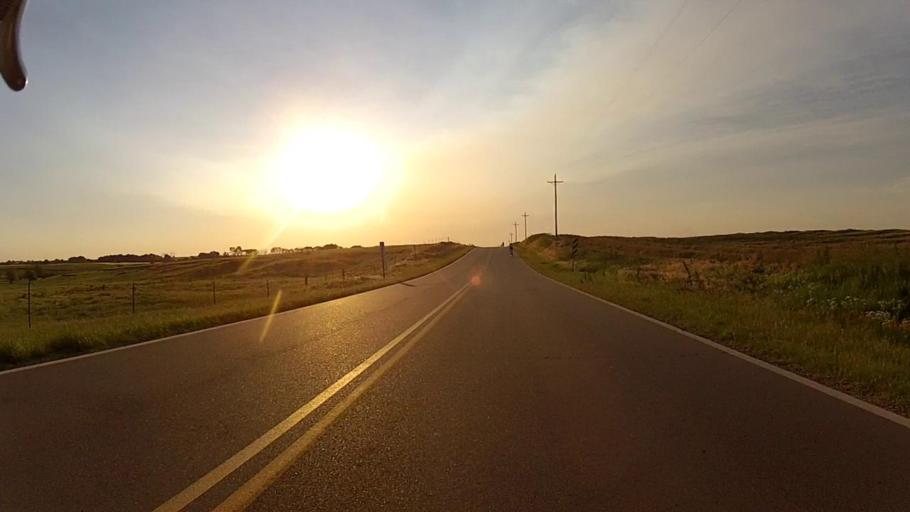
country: US
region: Kansas
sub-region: Harper County
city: Anthony
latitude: 37.1527
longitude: -97.9425
